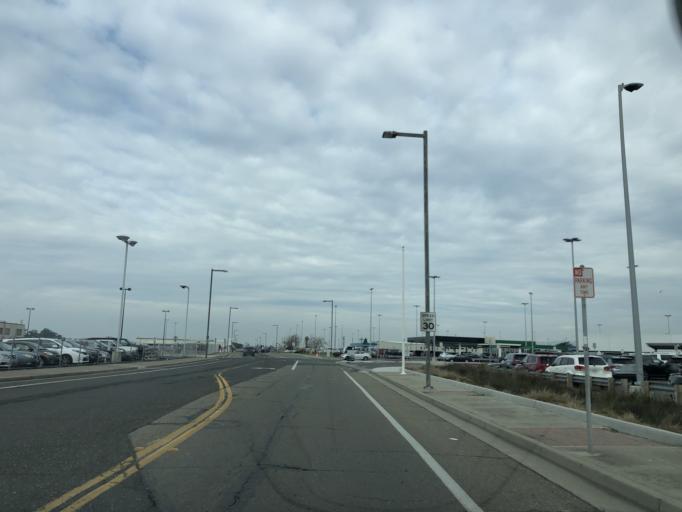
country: US
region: California
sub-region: Alameda County
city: Alameda
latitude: 37.7360
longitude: -122.2154
